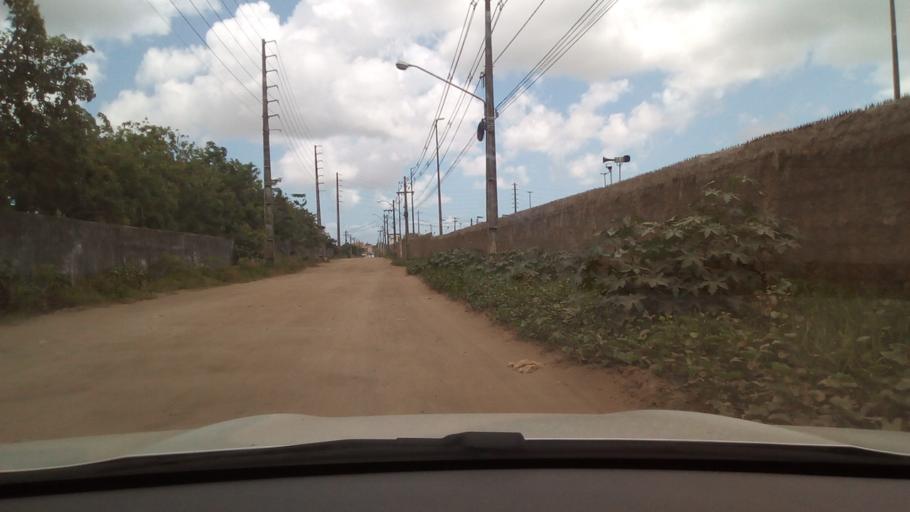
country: BR
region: Paraiba
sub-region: Joao Pessoa
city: Joao Pessoa
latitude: -7.1682
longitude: -34.8789
